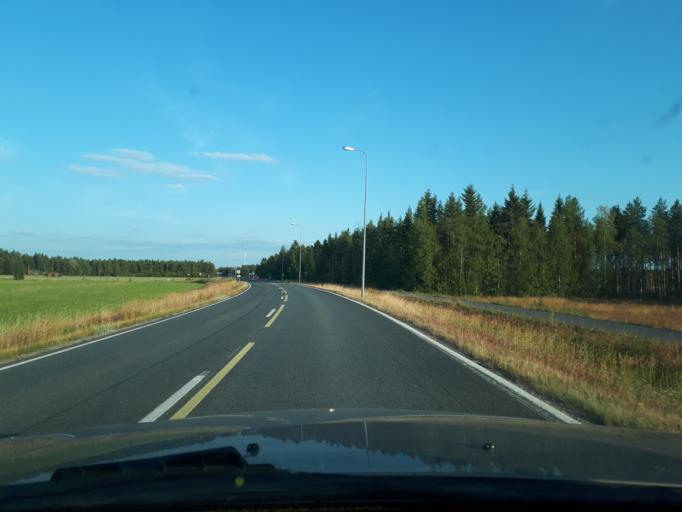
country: FI
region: Northern Ostrobothnia
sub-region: Oulu
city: Oulunsalo
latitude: 64.9802
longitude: 25.2737
